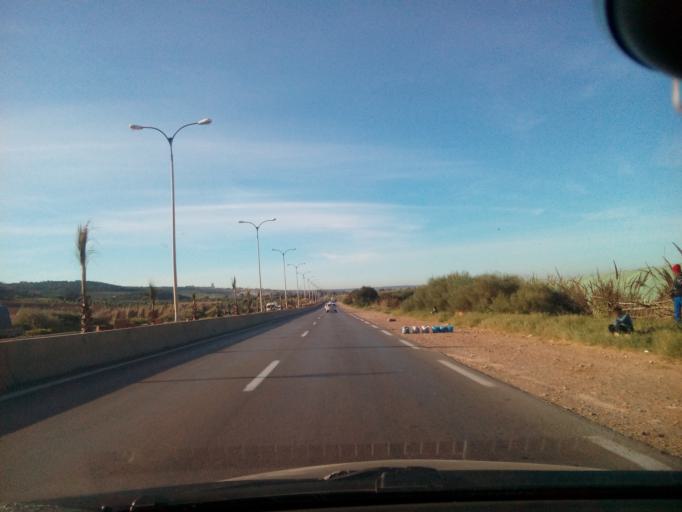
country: DZ
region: Mostaganem
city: Mostaganem
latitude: 35.8443
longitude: 0.0146
